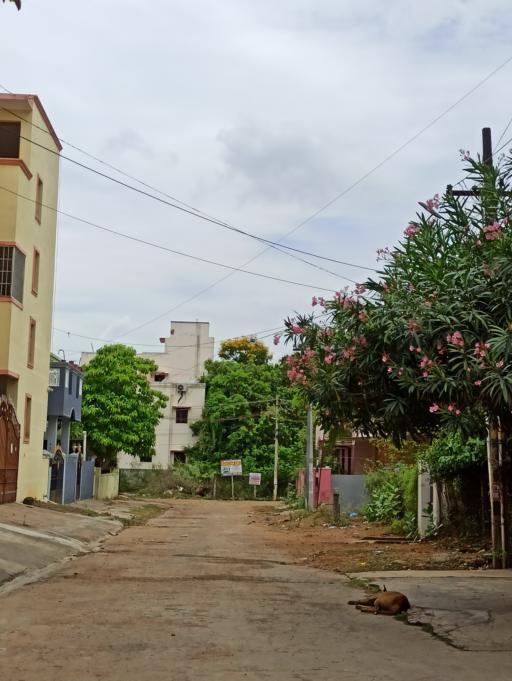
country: IN
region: Tamil Nadu
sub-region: Kancheepuram
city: Vandalur
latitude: 12.8966
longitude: 80.0639
